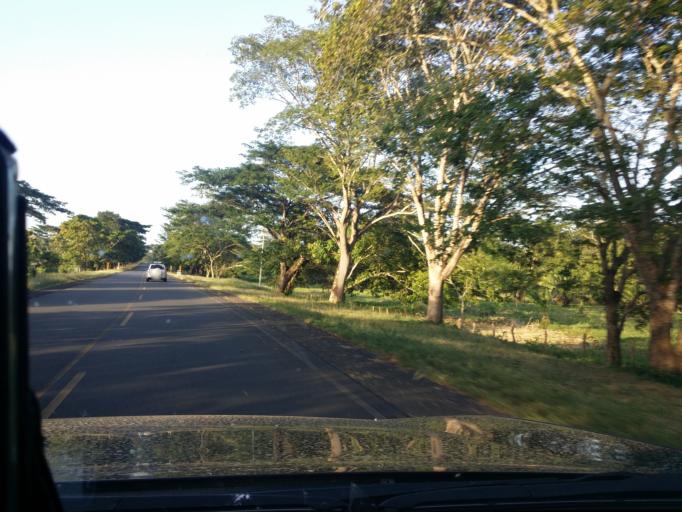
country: NI
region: Rio San Juan
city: San Miguelito
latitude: 11.4980
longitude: -84.8367
